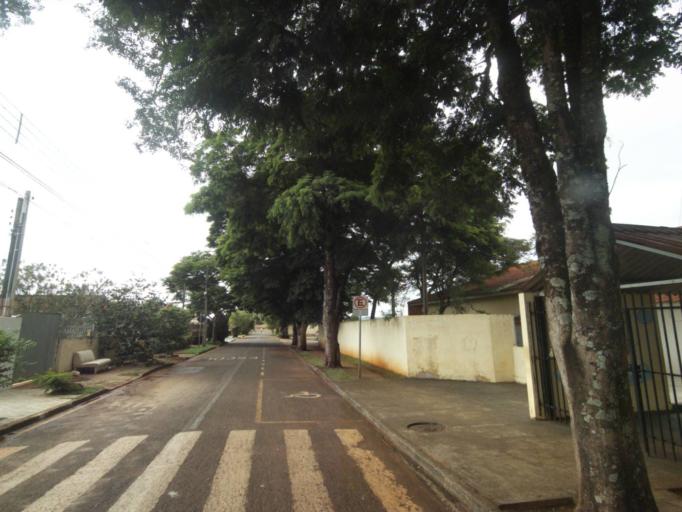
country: BR
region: Parana
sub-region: Campo Mourao
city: Campo Mourao
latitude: -24.0283
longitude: -52.3634
